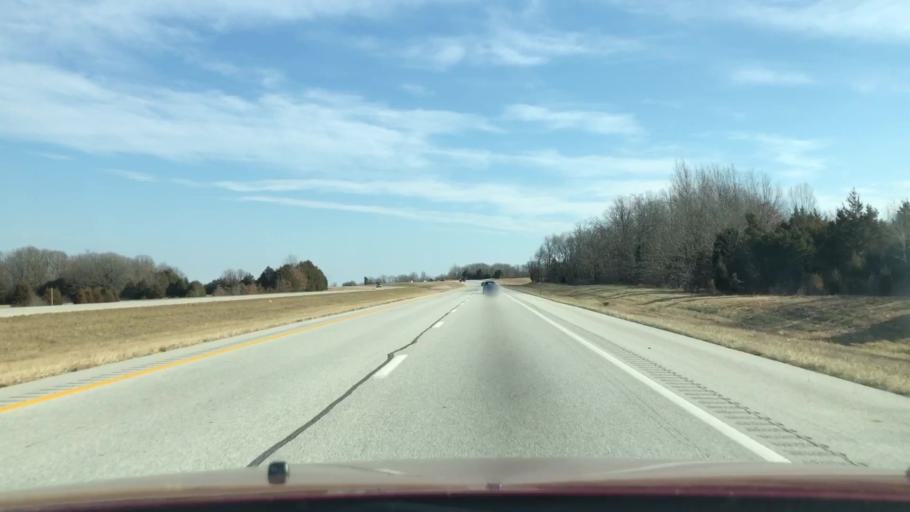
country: US
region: Missouri
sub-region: Webster County
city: Seymour
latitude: 37.1647
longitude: -92.8783
